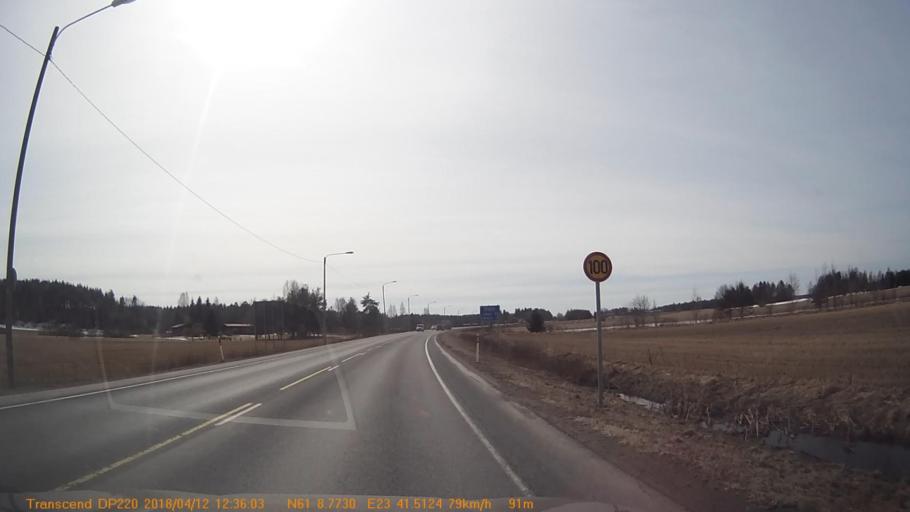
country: FI
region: Pirkanmaa
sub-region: Etelae-Pirkanmaa
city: Kylmaekoski
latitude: 61.1465
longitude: 23.6920
